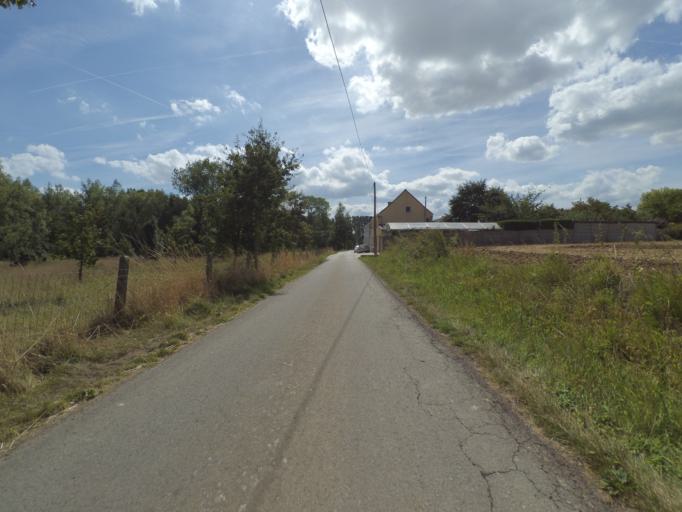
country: BE
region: Flanders
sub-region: Provincie Oost-Vlaanderen
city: Zottegem
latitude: 50.8525
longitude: 3.7629
